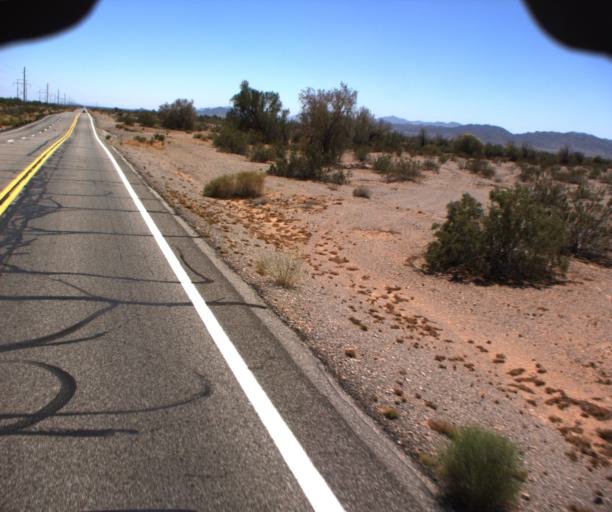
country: US
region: Arizona
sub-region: La Paz County
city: Quartzsite
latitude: 33.7811
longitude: -114.2170
